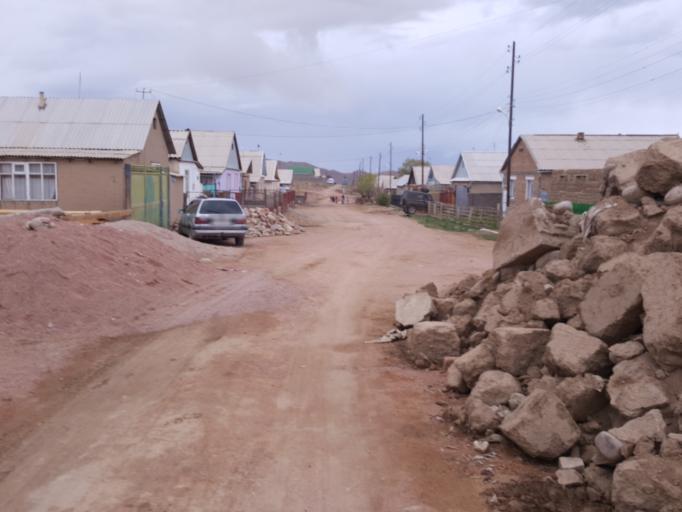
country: KG
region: Ysyk-Koel
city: Bokombayevskoye
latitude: 42.1092
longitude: 76.9808
